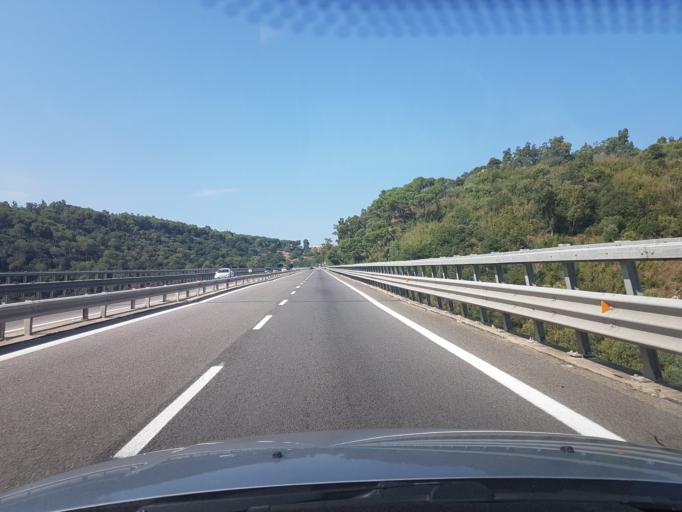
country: IT
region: Sardinia
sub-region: Provincia di Nuoro
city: Nuoro
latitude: 40.3343
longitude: 9.2971
